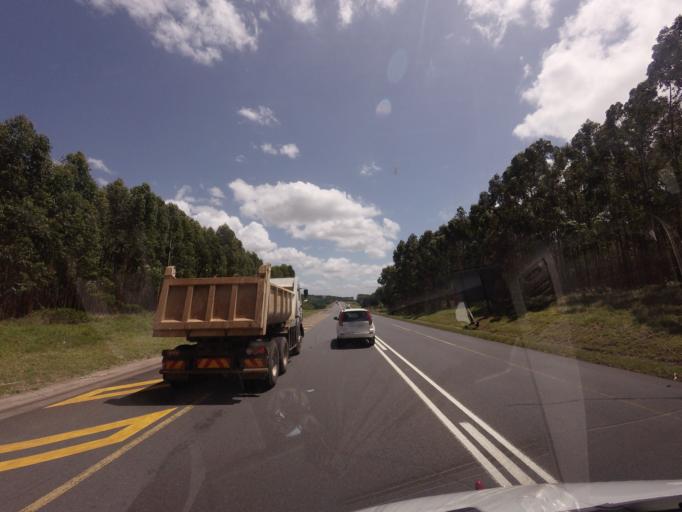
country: ZA
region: KwaZulu-Natal
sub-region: uThungulu District Municipality
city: KwaMbonambi
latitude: -28.5883
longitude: 32.0995
